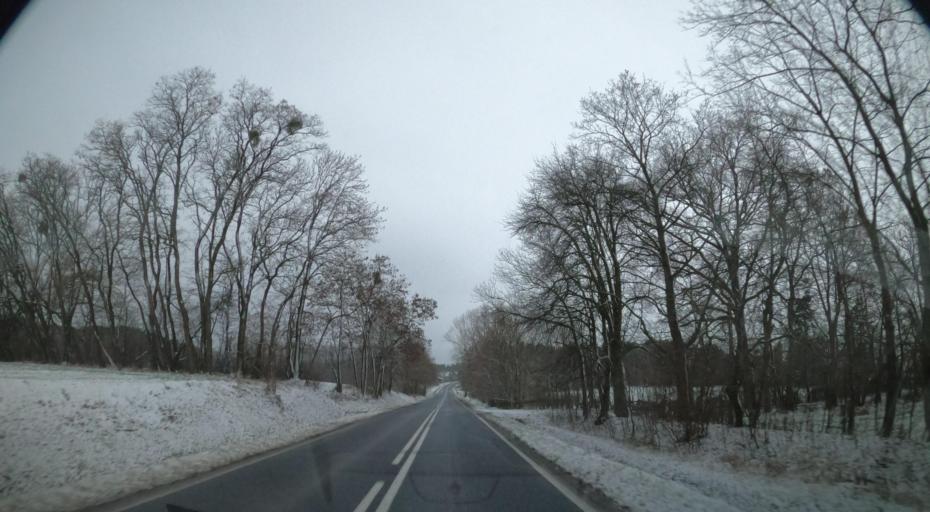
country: PL
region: Masovian Voivodeship
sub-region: Powiat plocki
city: Nowy Duninow
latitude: 52.6088
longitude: 19.4774
